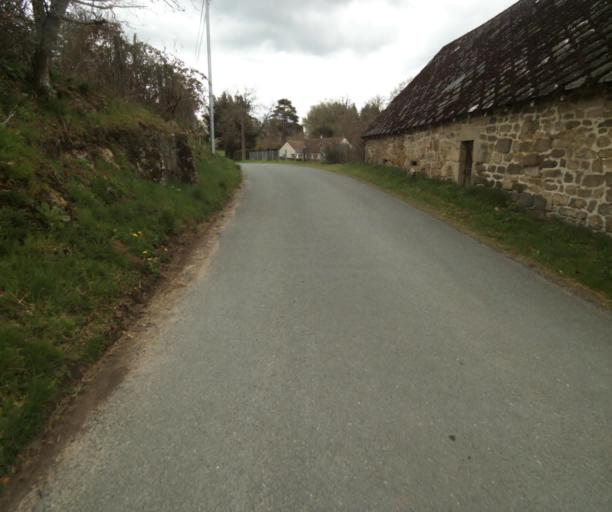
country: FR
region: Limousin
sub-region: Departement de la Correze
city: Correze
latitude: 45.3174
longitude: 1.9306
